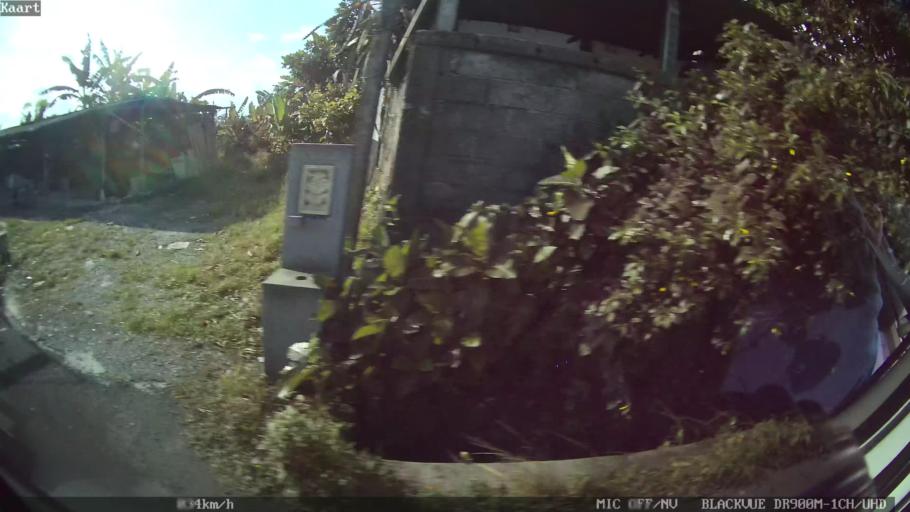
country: ID
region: Bali
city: Banjar Desa
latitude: -8.5796
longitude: 115.2301
